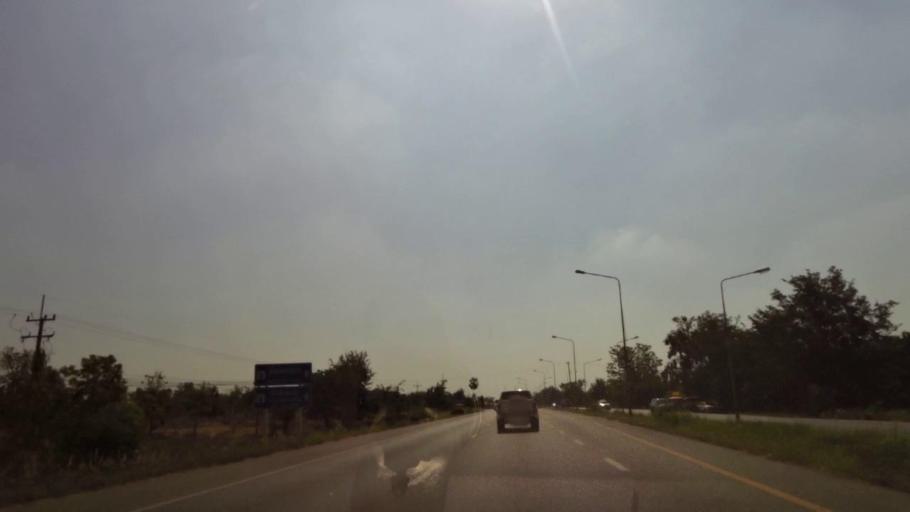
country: TH
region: Phichit
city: Wachira Barami
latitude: 16.4272
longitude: 100.1445
